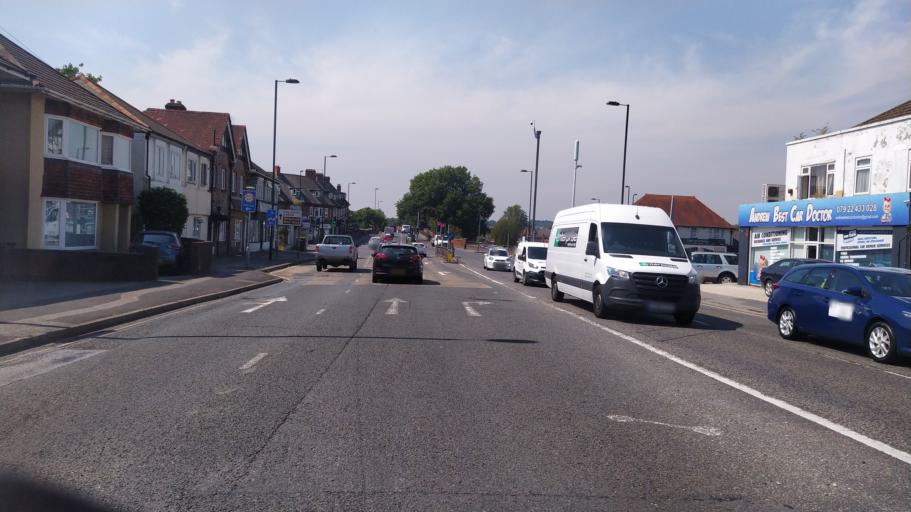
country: GB
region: England
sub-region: Southampton
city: Southampton
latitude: 50.9175
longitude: -1.3739
